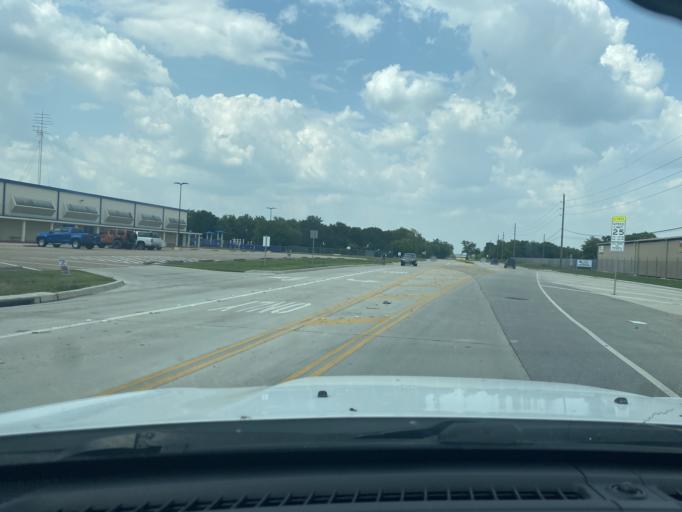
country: US
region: Texas
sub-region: Fort Bend County
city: Greatwood
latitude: 29.5406
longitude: -95.7248
